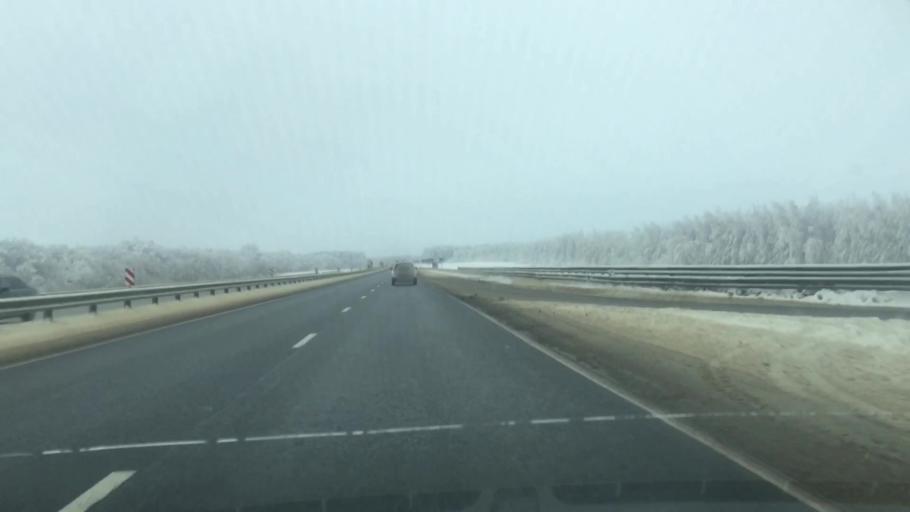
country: RU
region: Lipetsk
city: Zadonsk
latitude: 52.5015
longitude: 38.7554
